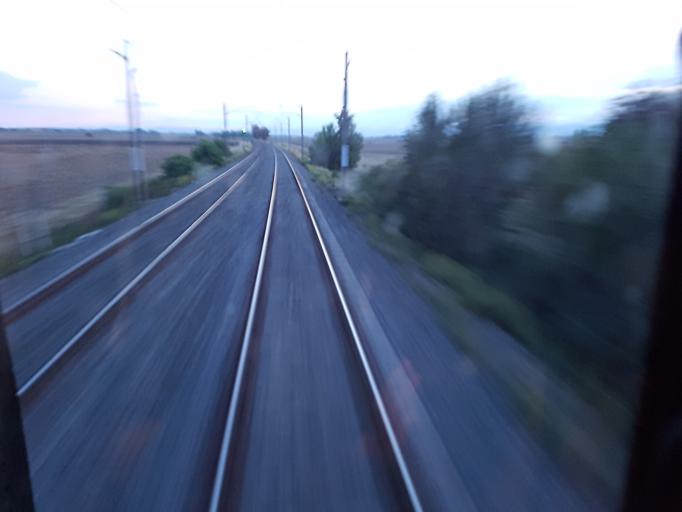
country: FR
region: Auvergne
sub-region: Departement du Puy-de-Dome
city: Ennezat
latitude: 45.9553
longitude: 3.2498
